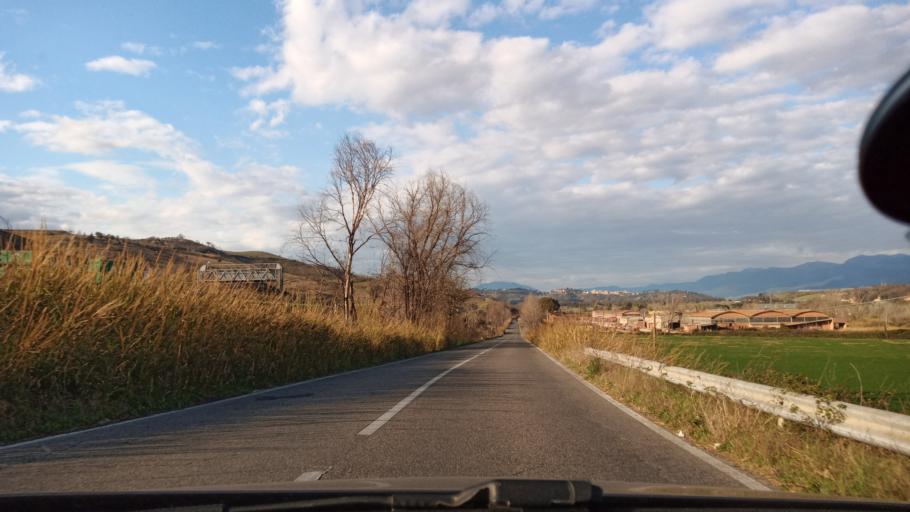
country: IT
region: Latium
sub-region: Citta metropolitana di Roma Capitale
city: Civitella San Paolo
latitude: 42.1882
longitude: 12.6037
